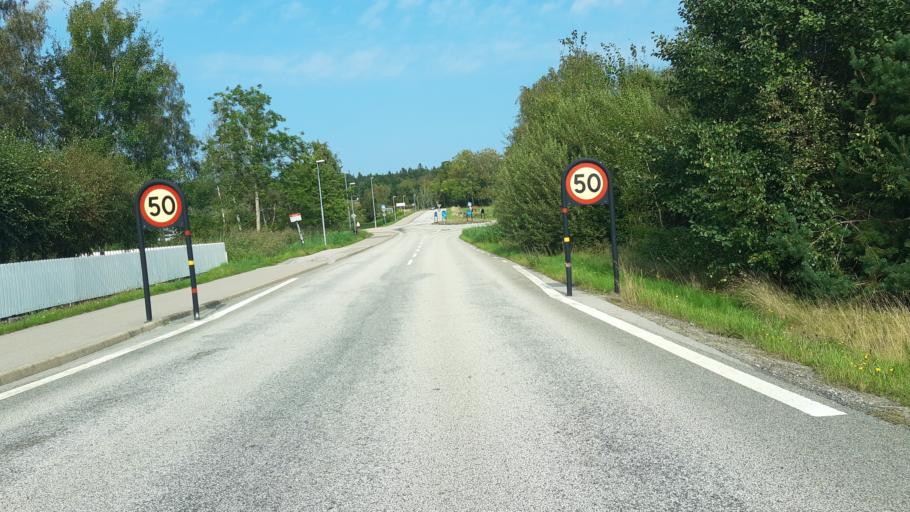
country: SE
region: Blekinge
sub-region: Ronneby Kommun
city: Ronneby
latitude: 56.1754
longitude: 15.2791
